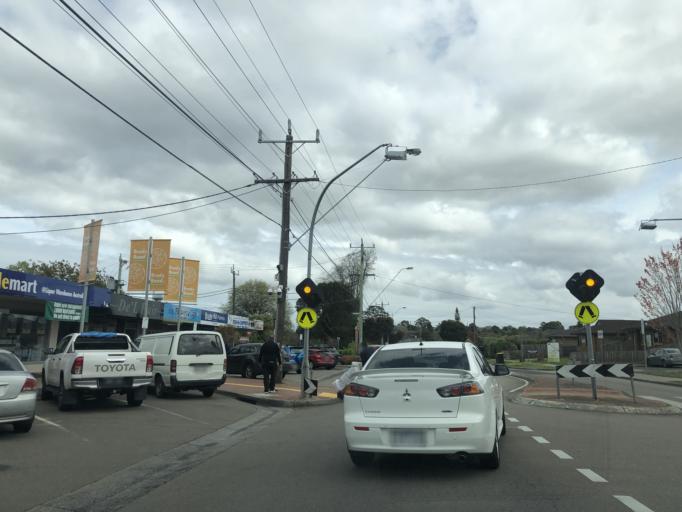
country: AU
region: Victoria
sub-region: Greater Dandenong
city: Dandenong North
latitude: -37.9541
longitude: 145.2127
